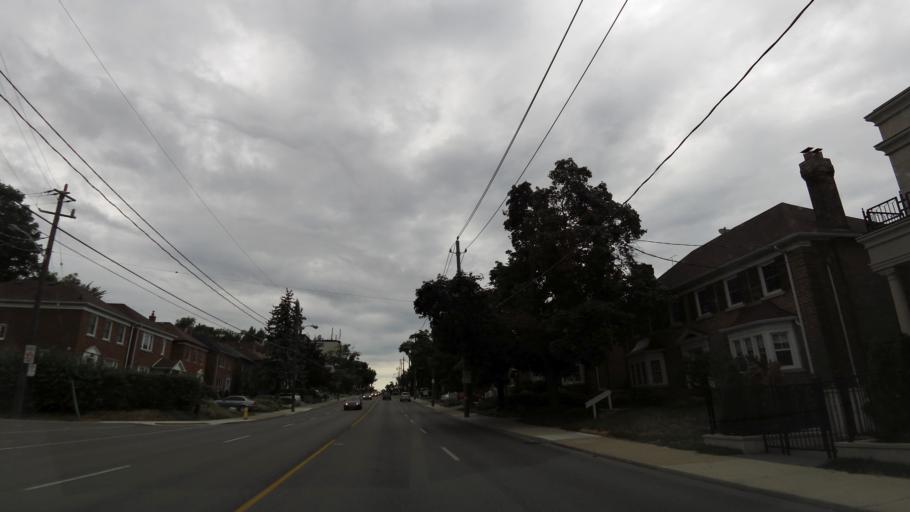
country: CA
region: Ontario
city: Toronto
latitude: 43.6959
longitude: -79.4235
